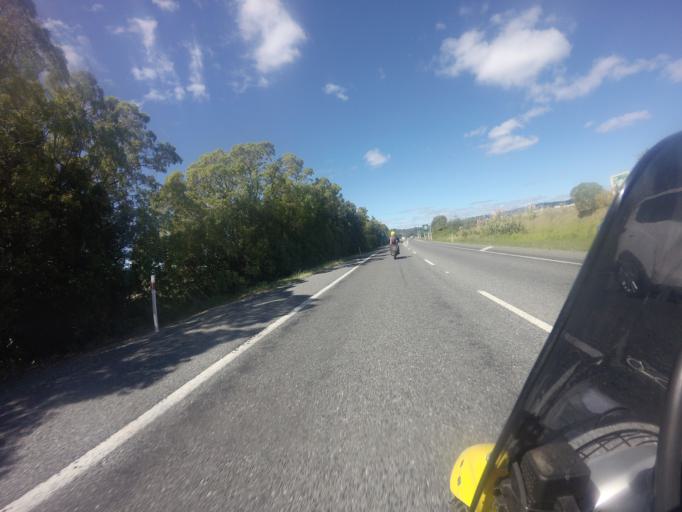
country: NZ
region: Bay of Plenty
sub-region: Whakatane District
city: Whakatane
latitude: -37.9515
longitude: 176.9611
